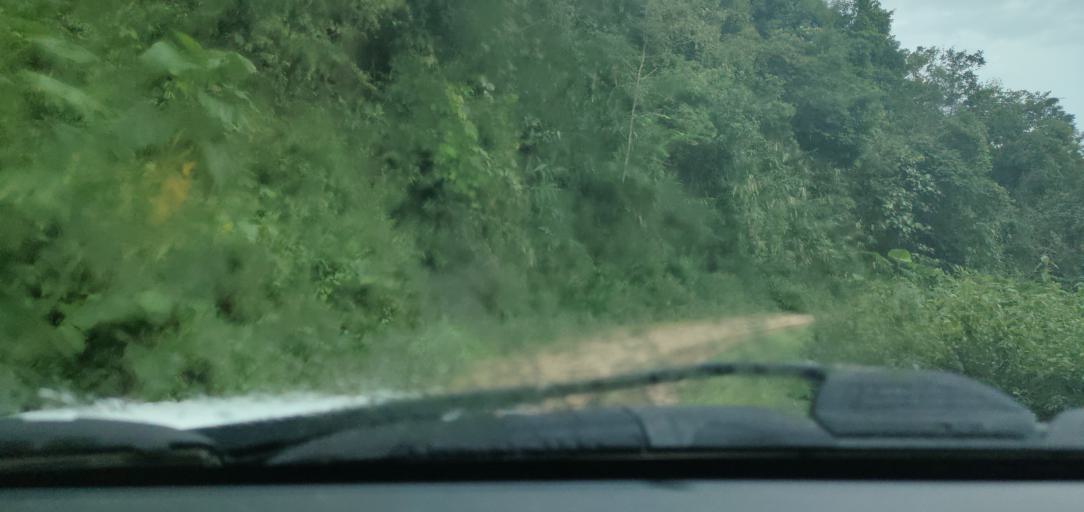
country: LA
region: Phongsali
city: Phongsali
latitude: 21.4462
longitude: 102.3154
